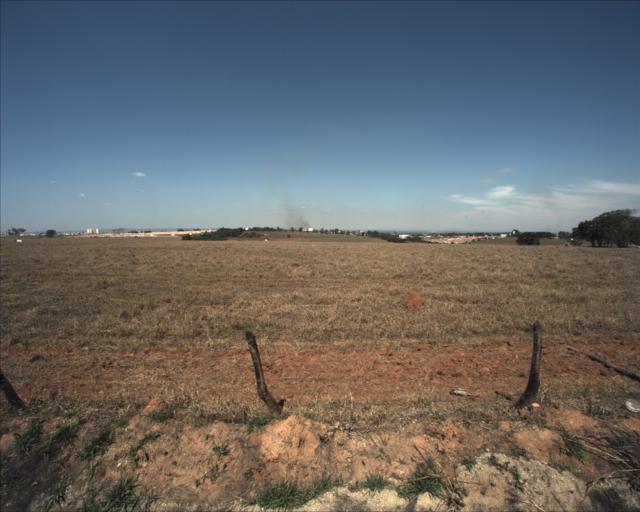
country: BR
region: Sao Paulo
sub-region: Aracoiaba Da Serra
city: Aracoiaba da Serra
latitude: -23.4862
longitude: -47.5432
